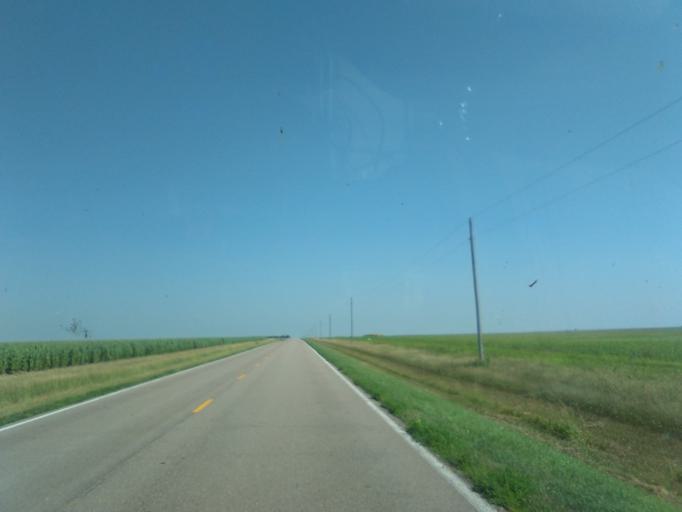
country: US
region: Nebraska
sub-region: Dundy County
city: Benkelman
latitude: 39.8332
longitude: -101.5411
